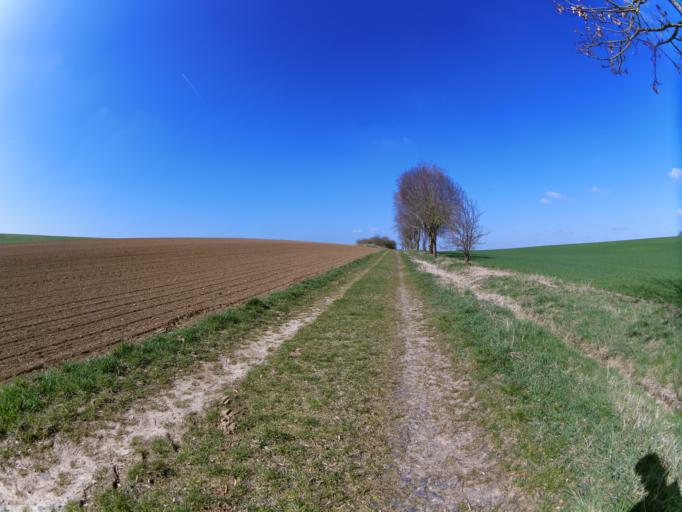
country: DE
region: Bavaria
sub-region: Regierungsbezirk Unterfranken
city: Prosselsheim
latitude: 49.8383
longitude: 10.1347
